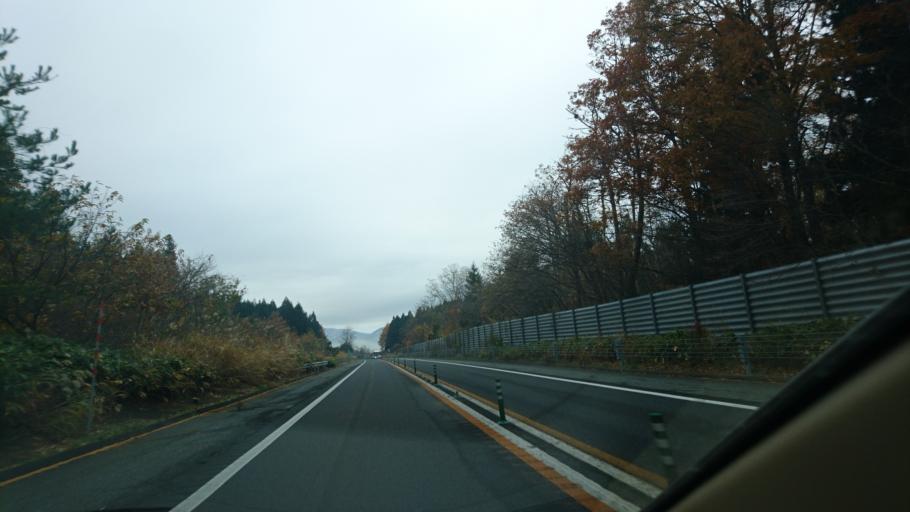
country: JP
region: Iwate
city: Kitakami
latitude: 39.2807
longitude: 141.0304
